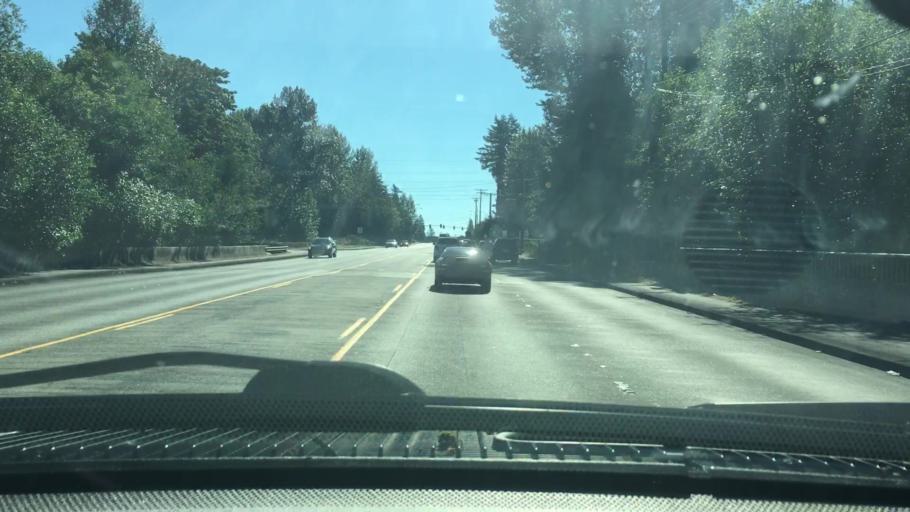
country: US
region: Washington
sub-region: King County
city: Covington
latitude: 47.3580
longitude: -122.1294
